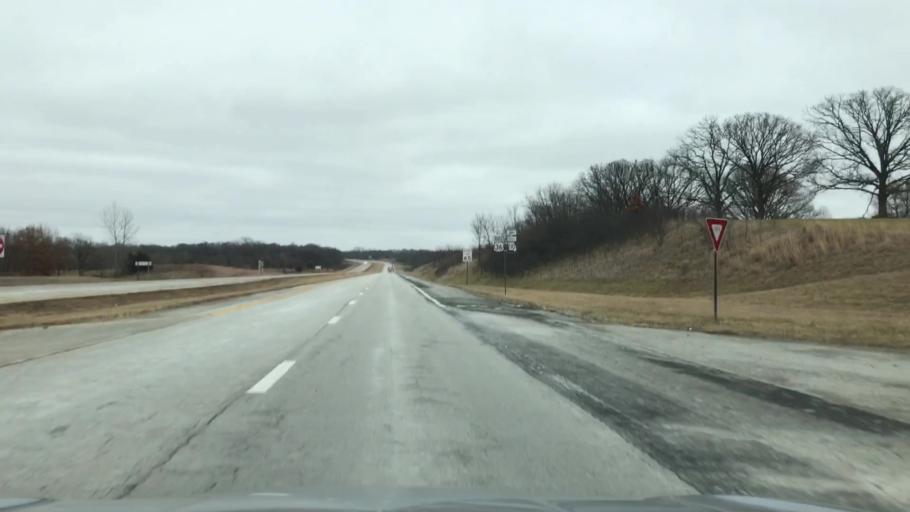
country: US
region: Missouri
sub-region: Caldwell County
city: Hamilton
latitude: 39.7414
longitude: -94.0378
